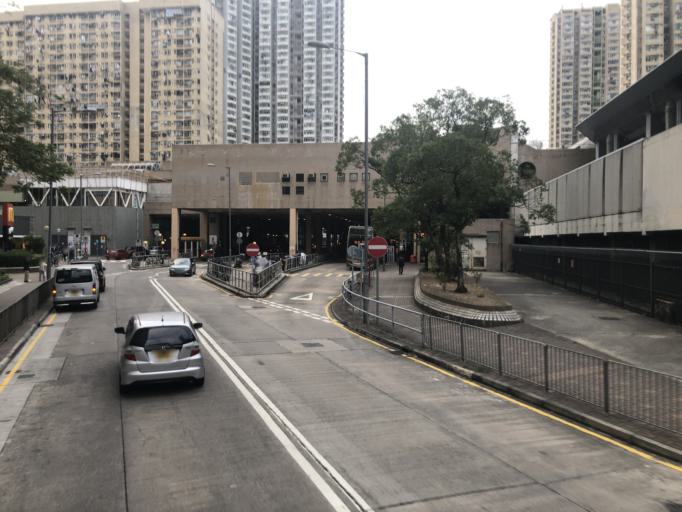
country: HK
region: Tai Po
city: Tai Po
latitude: 22.4500
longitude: 114.1617
